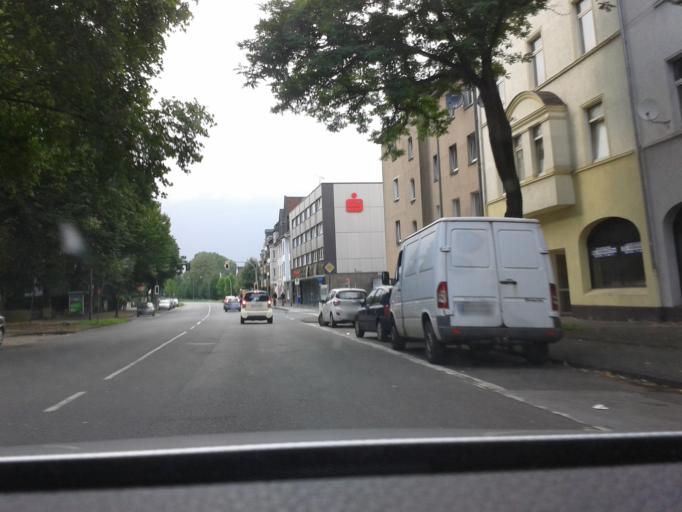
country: DE
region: North Rhine-Westphalia
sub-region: Regierungsbezirk Dusseldorf
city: Hochfeld
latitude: 51.4205
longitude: 6.7061
